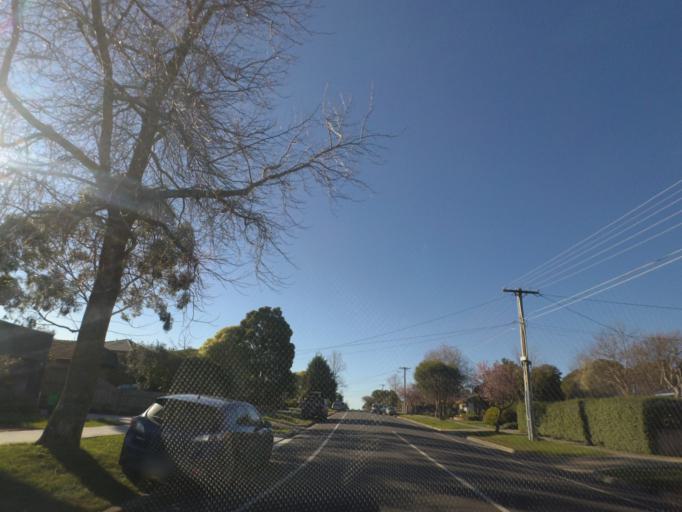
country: AU
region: Victoria
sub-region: Yarra Ranges
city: Kilsyth
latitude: -37.8017
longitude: 145.3125
